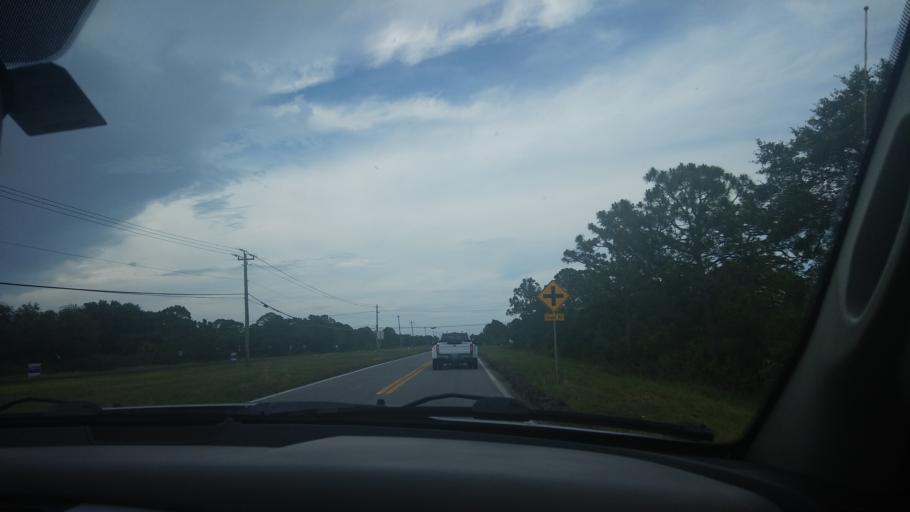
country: US
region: Florida
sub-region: Brevard County
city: Grant-Valkaria
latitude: 27.9229
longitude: -80.6230
